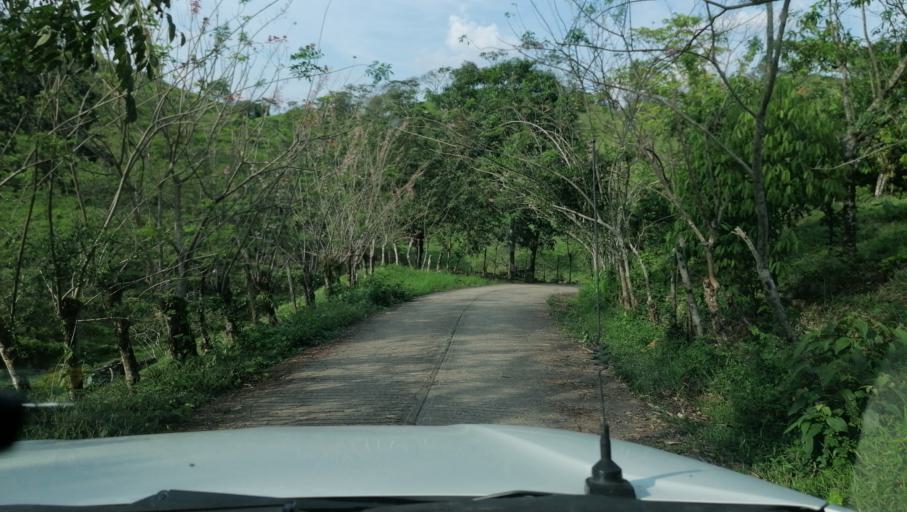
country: MX
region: Chiapas
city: Pichucalco
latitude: 17.4809
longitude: -93.2226
